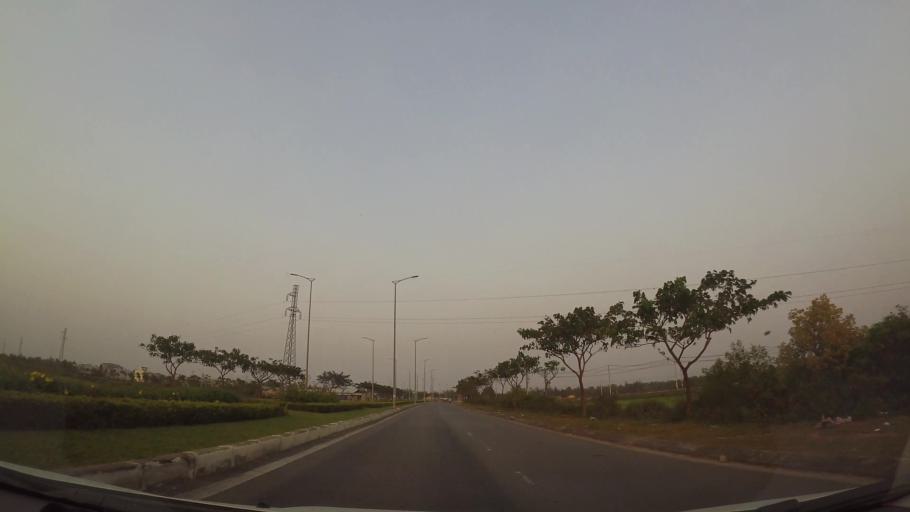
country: VN
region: Da Nang
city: Ngu Hanh Son
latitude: 15.9757
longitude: 108.2312
